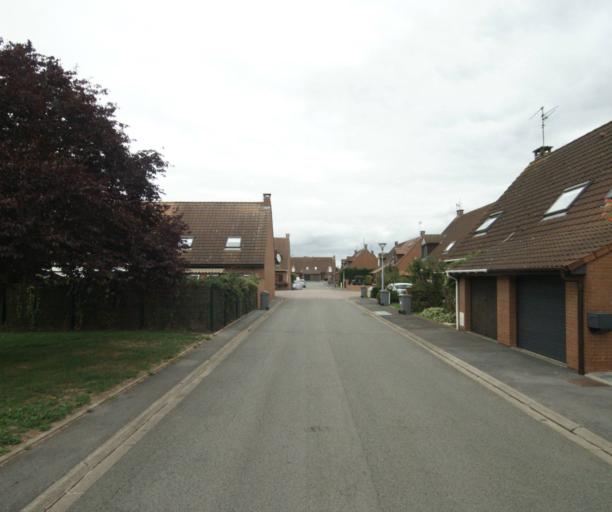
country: FR
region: Nord-Pas-de-Calais
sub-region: Departement du Nord
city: Fretin
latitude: 50.5547
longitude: 3.1258
